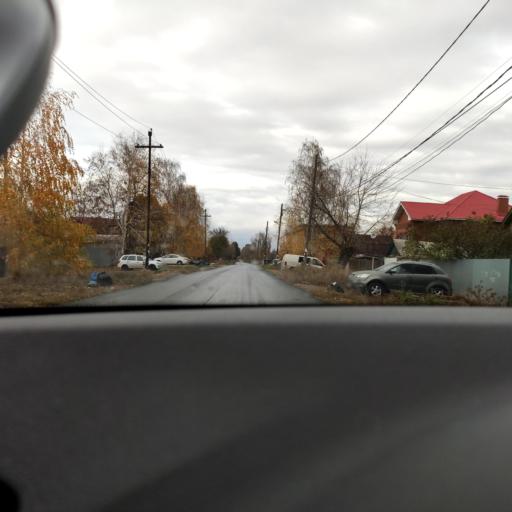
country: RU
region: Samara
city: Smyshlyayevka
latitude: 53.2411
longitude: 50.3273
